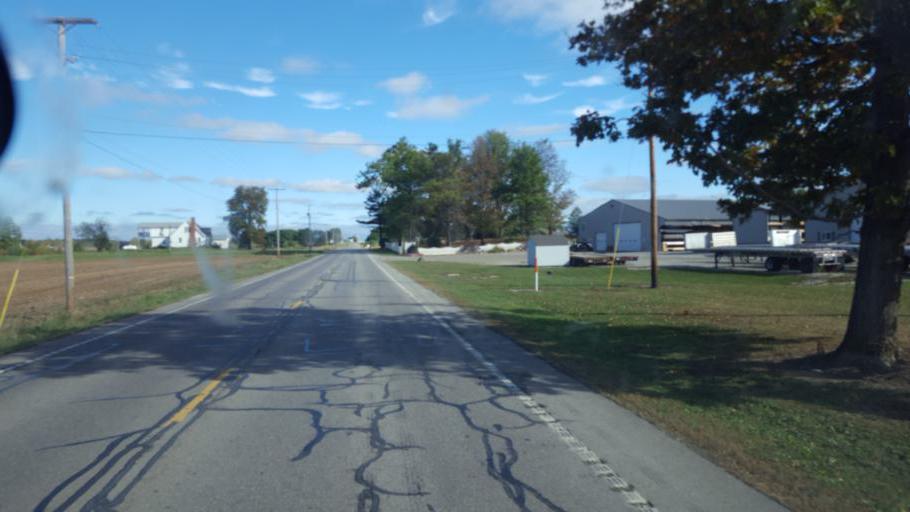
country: US
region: Ohio
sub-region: Huron County
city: Greenwich
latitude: 40.9841
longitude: -82.4894
